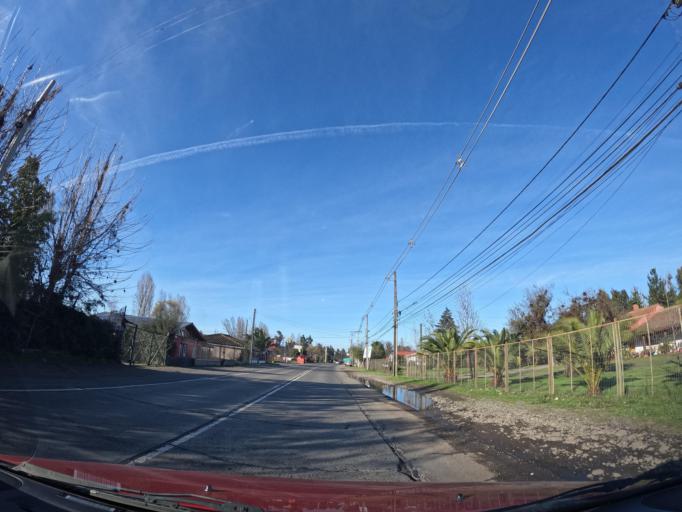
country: CL
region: Maule
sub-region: Provincia de Linares
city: San Javier
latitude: -35.5719
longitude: -71.6897
